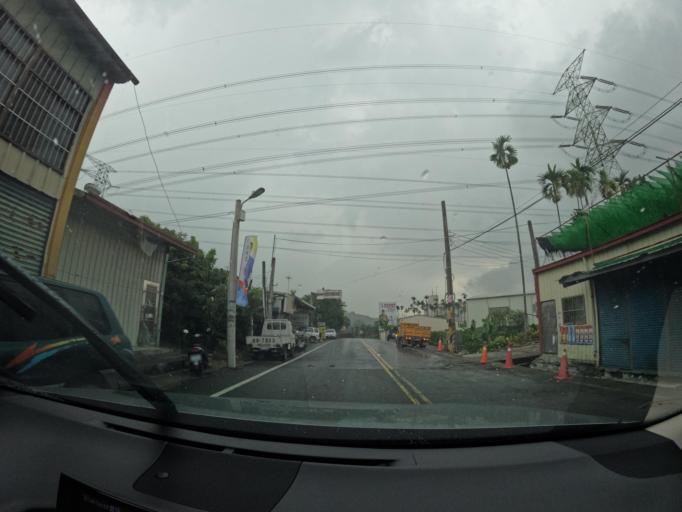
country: TW
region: Taiwan
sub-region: Nantou
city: Nantou
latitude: 23.8807
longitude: 120.7610
